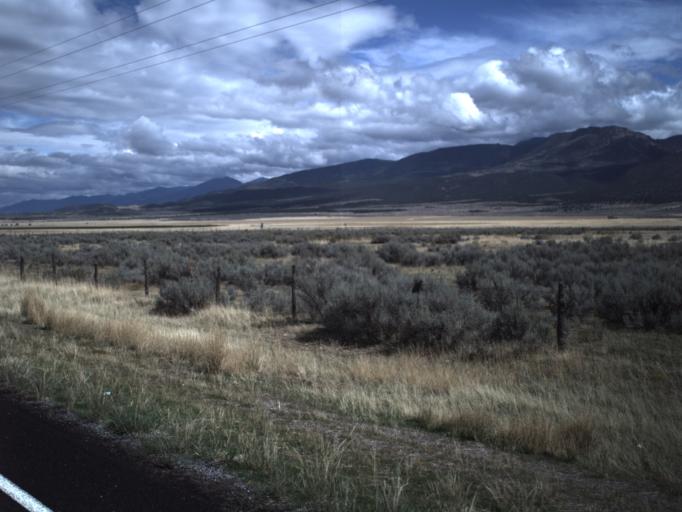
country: US
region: Utah
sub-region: Millard County
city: Fillmore
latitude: 38.8169
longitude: -112.4351
